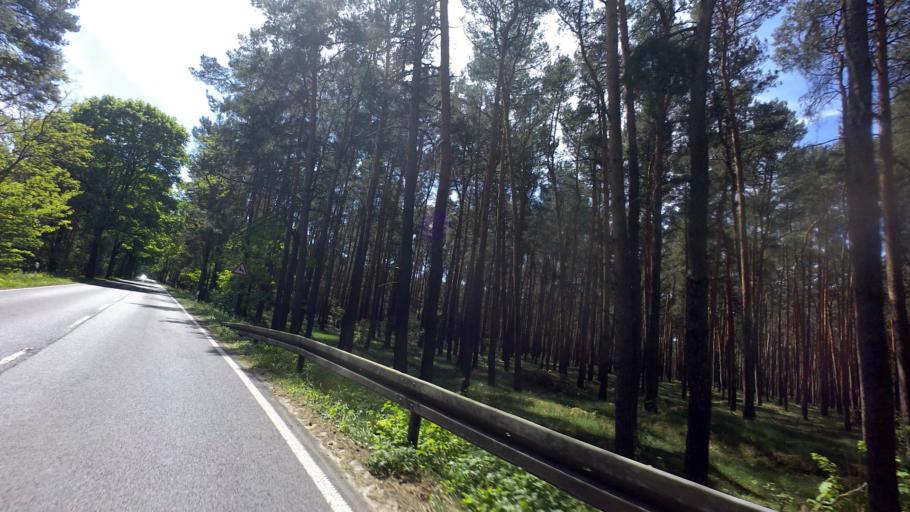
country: DE
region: Brandenburg
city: Luckenwalde
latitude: 52.1336
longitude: 13.1273
